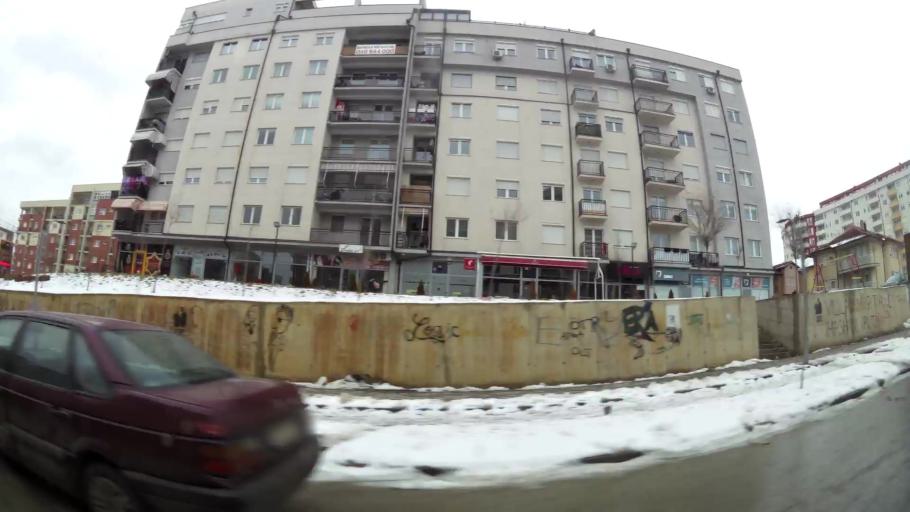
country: XK
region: Pristina
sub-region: Komuna e Prishtines
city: Pristina
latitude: 42.6507
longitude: 21.1781
